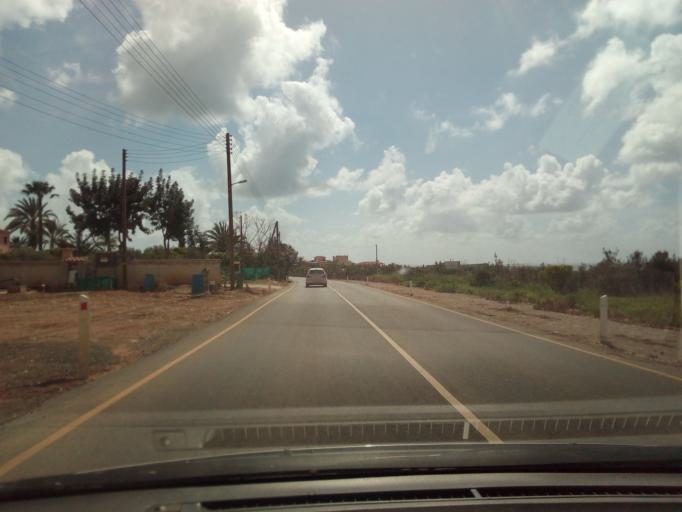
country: CY
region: Pafos
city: Pegeia
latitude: 34.8616
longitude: 32.3798
